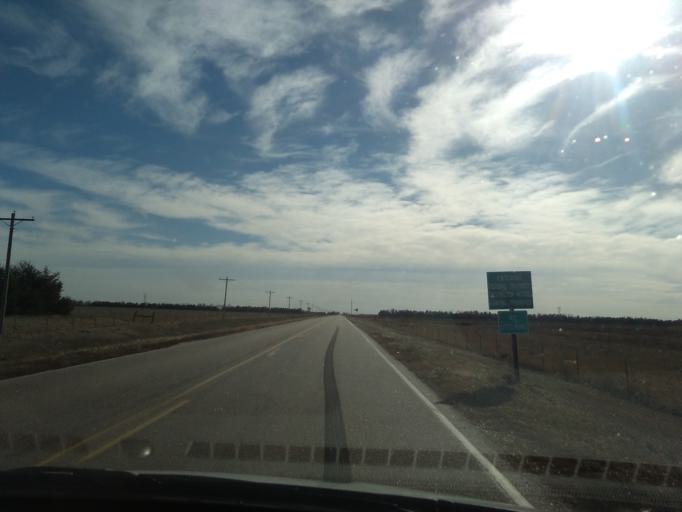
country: US
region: Nebraska
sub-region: Adams County
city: Hastings
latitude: 40.5675
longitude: -98.2413
